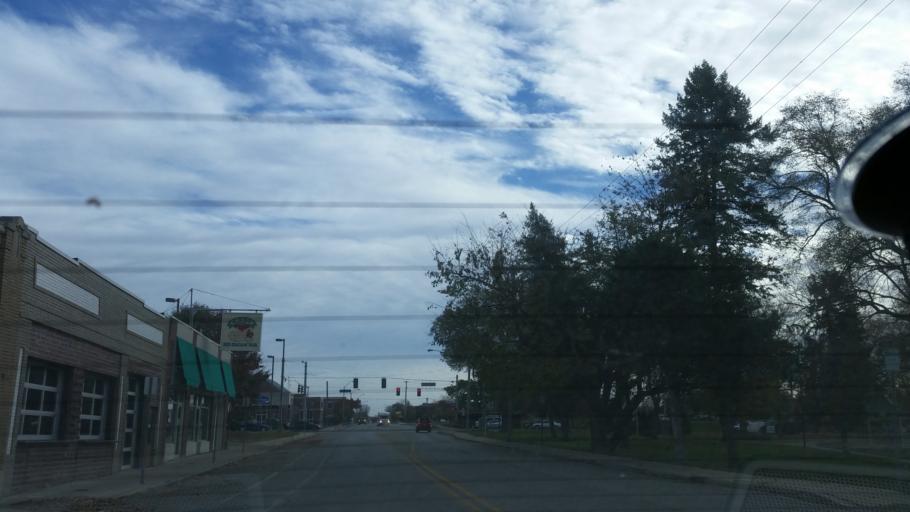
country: US
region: Indiana
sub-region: Howard County
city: Kokomo
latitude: 40.4855
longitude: -86.1350
